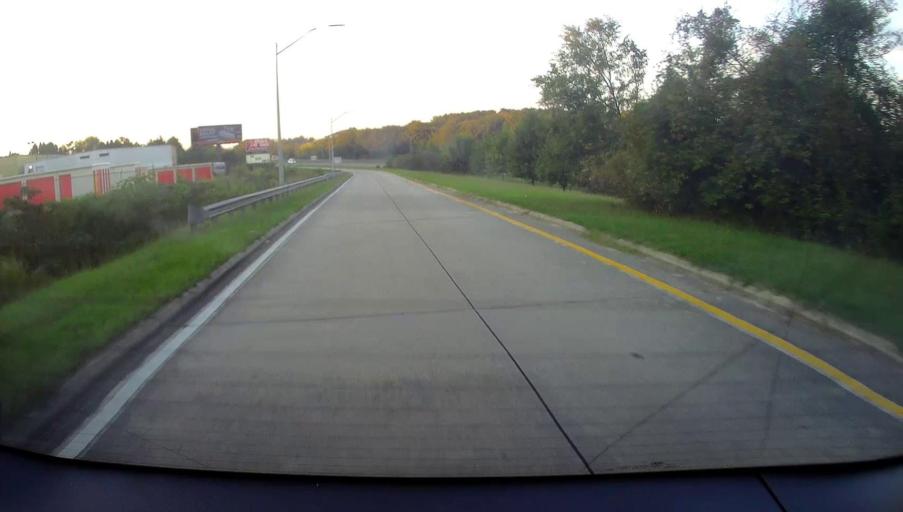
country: US
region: Georgia
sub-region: Bibb County
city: Macon
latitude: 32.8240
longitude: -83.6558
